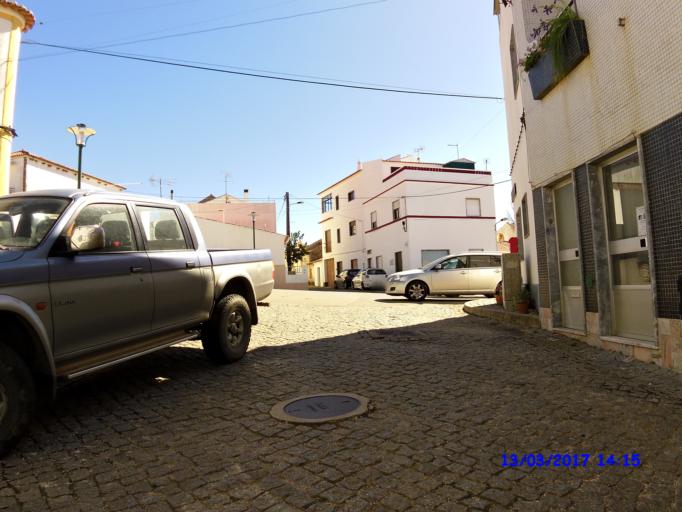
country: PT
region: Faro
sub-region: Monchique
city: Monchique
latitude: 37.3096
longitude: -8.6666
